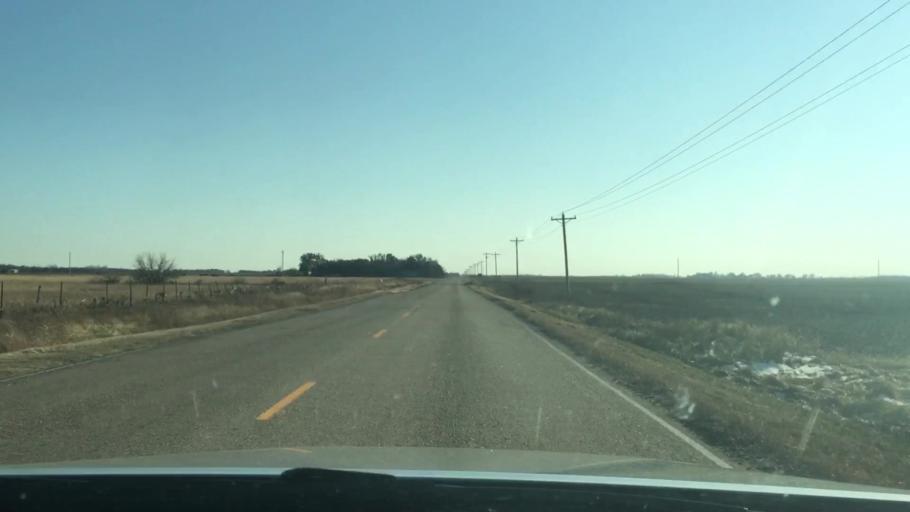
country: US
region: Kansas
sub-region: Reno County
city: Nickerson
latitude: 38.2348
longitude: -98.0877
